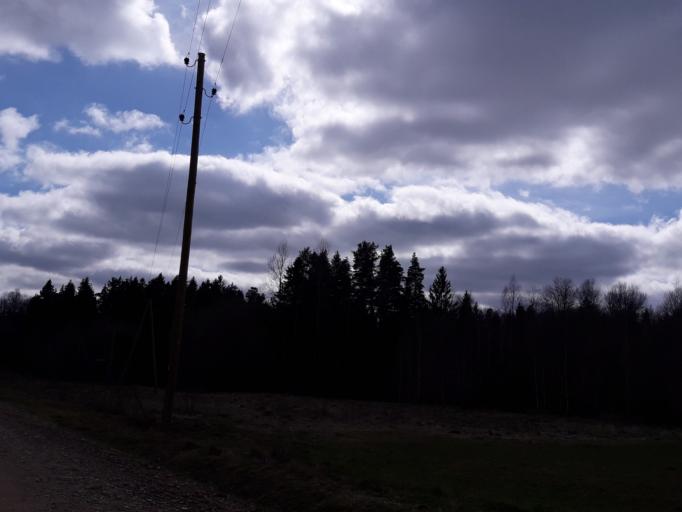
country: LV
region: Talsu Rajons
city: Sabile
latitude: 56.9091
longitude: 22.3993
